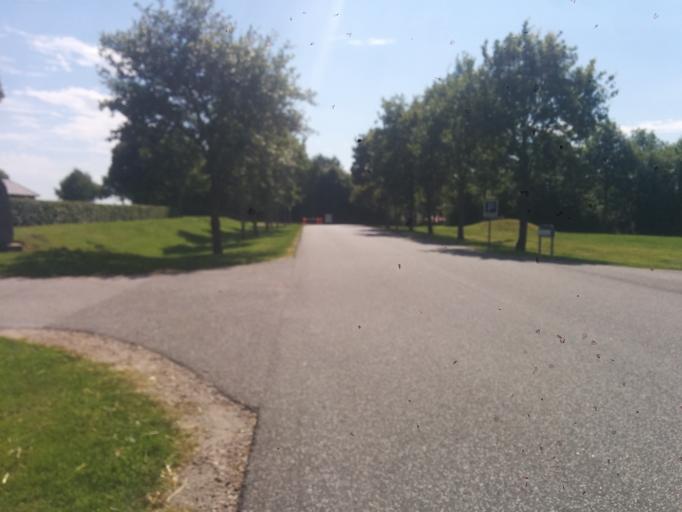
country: DK
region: Central Jutland
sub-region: Viborg Kommune
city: Bjerringbro
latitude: 56.4876
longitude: 9.5823
